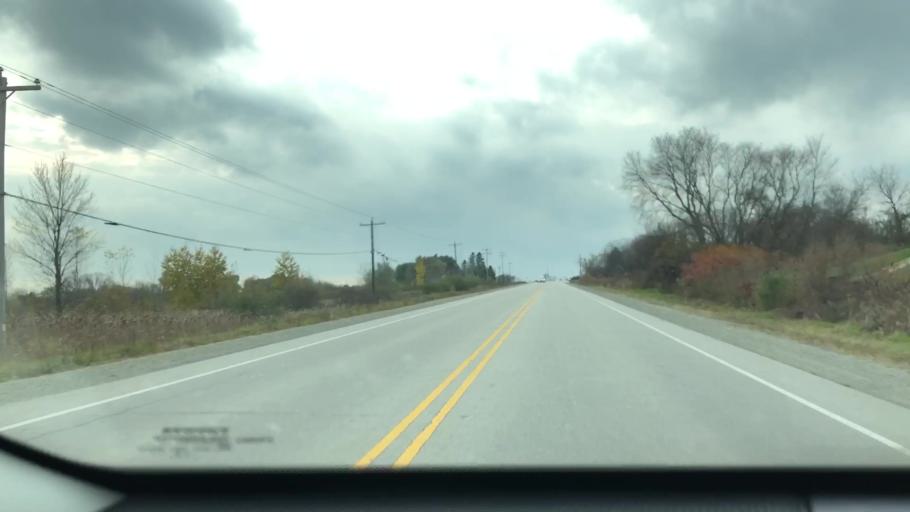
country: US
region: Wisconsin
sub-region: Brown County
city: Oneida
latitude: 44.5097
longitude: -88.1645
